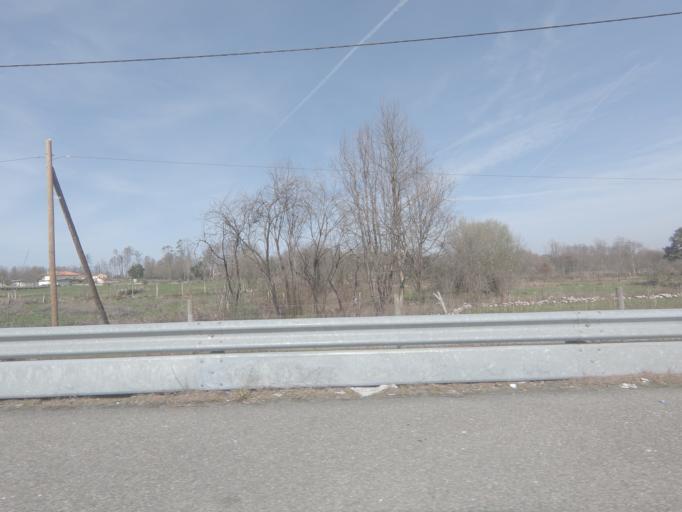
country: PT
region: Viseu
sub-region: Oliveira de Frades
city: Oliveira de Frades
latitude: 40.6874
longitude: -8.2336
